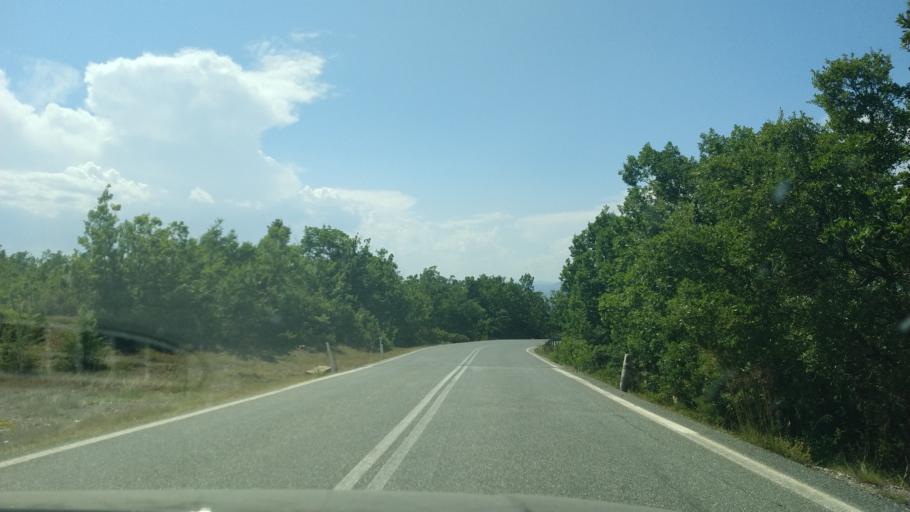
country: GR
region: West Macedonia
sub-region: Nomos Grevenon
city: Grevena
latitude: 40.0214
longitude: 21.4854
